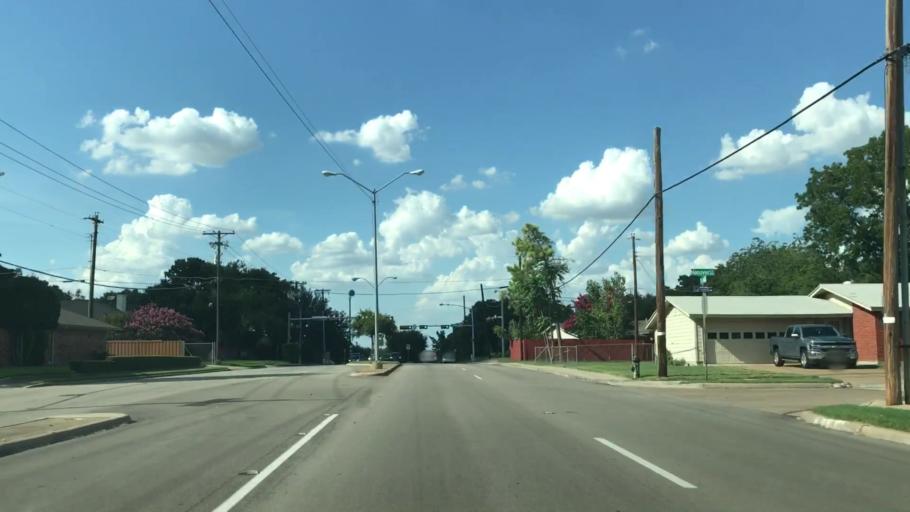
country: US
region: Texas
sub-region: Dallas County
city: Irving
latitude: 32.8527
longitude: -96.9504
